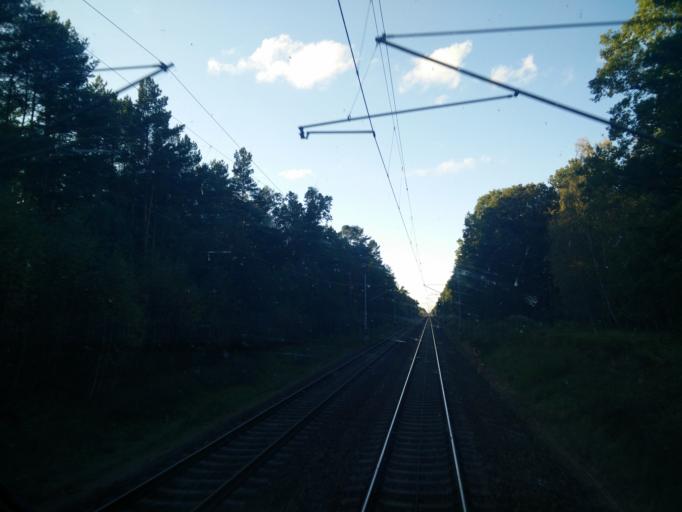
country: DE
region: Brandenburg
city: Dreetz
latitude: 52.8258
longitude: 12.4909
